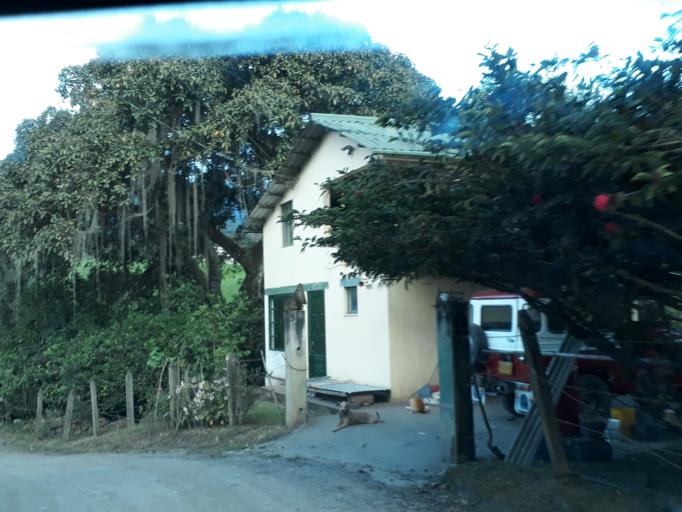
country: CO
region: Cundinamarca
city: Pacho
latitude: 5.1497
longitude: -74.1592
